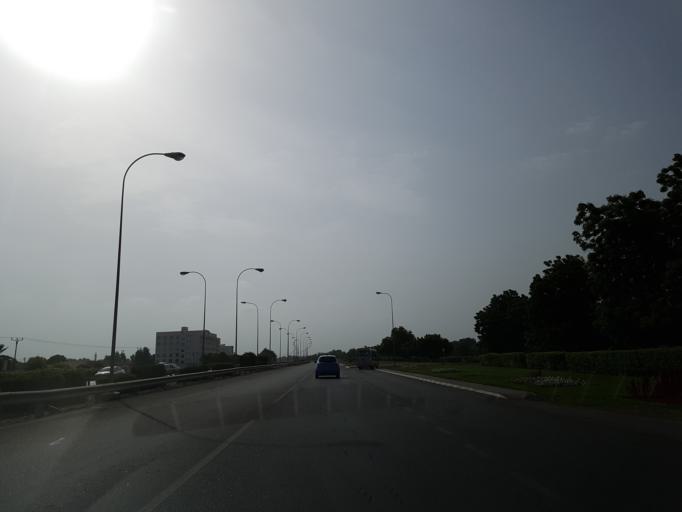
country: OM
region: Al Batinah
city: Al Sohar
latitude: 24.3999
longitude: 56.6649
